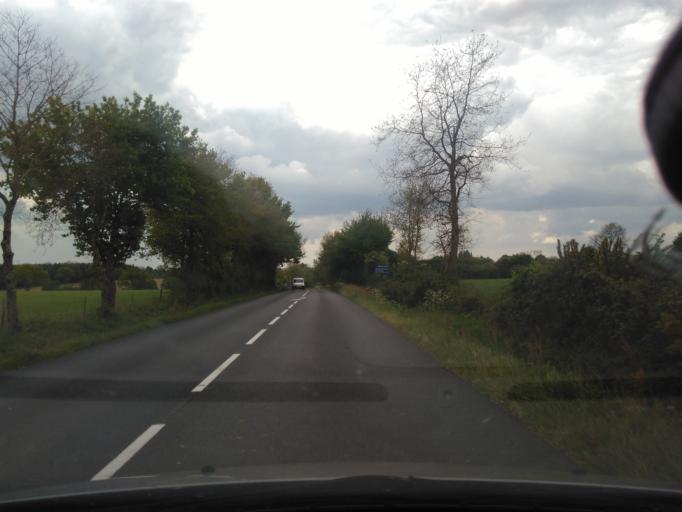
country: FR
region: Pays de la Loire
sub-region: Departement de la Vendee
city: Mouilleron-le-Captif
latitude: 46.7060
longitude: -1.4160
